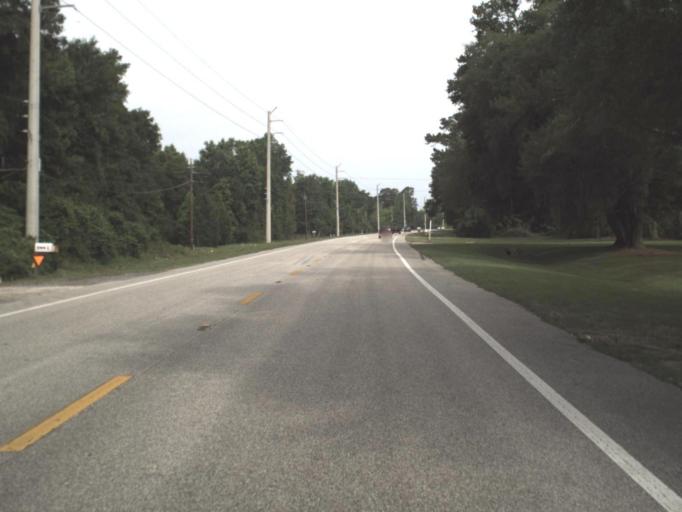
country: US
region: Florida
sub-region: Saint Johns County
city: Saint Augustine
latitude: 29.9484
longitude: -81.4493
